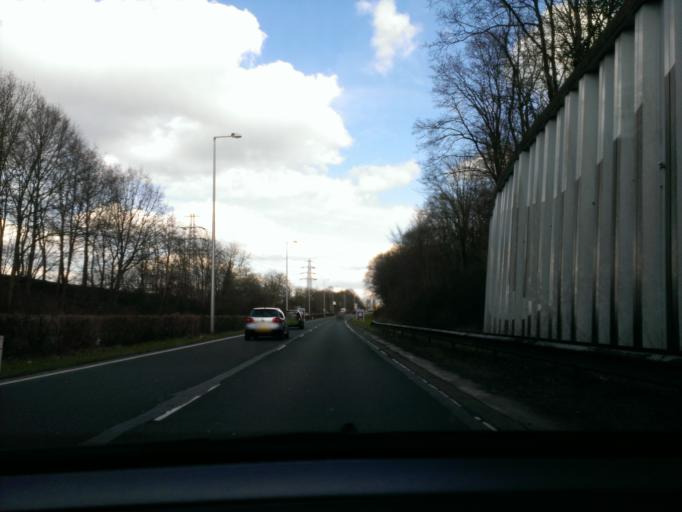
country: NL
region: Overijssel
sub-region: Gemeente Enschede
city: Enschede
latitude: 52.2189
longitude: 6.8571
